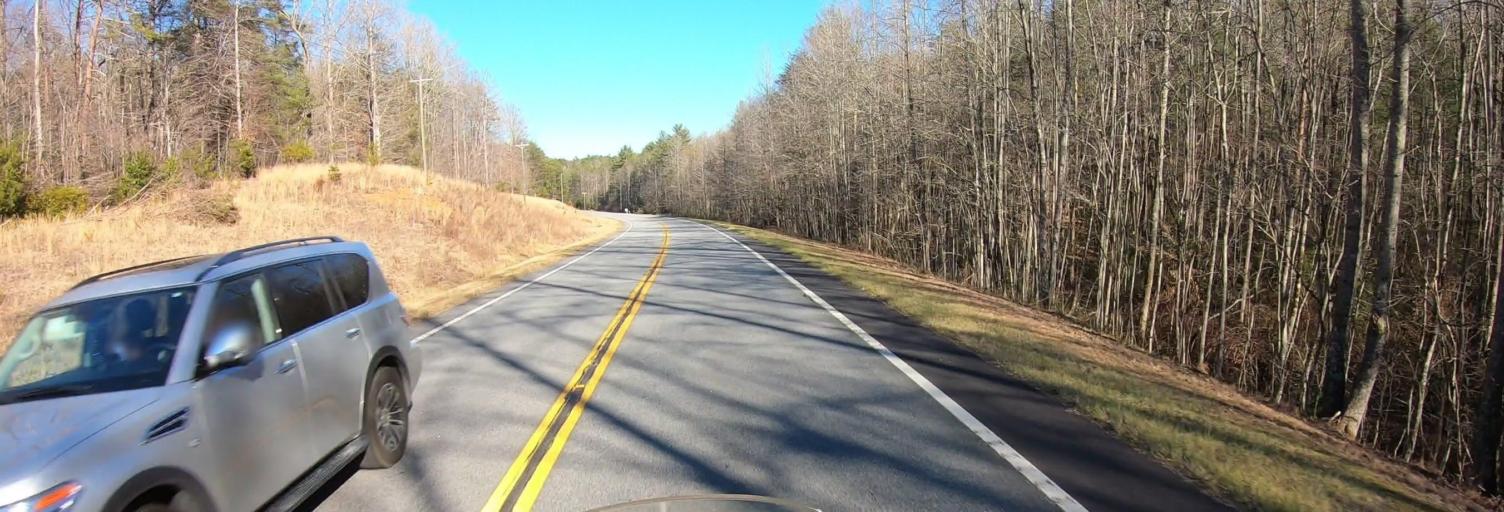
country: US
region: South Carolina
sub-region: Pickens County
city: Pickens
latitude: 34.9850
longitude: -82.7634
